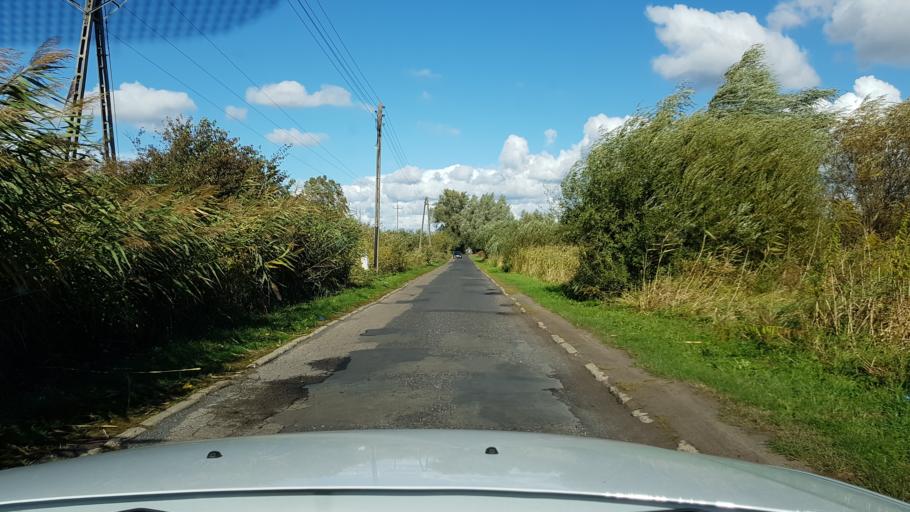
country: PL
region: West Pomeranian Voivodeship
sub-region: Powiat gryfinski
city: Gryfino
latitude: 53.2684
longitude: 14.4976
